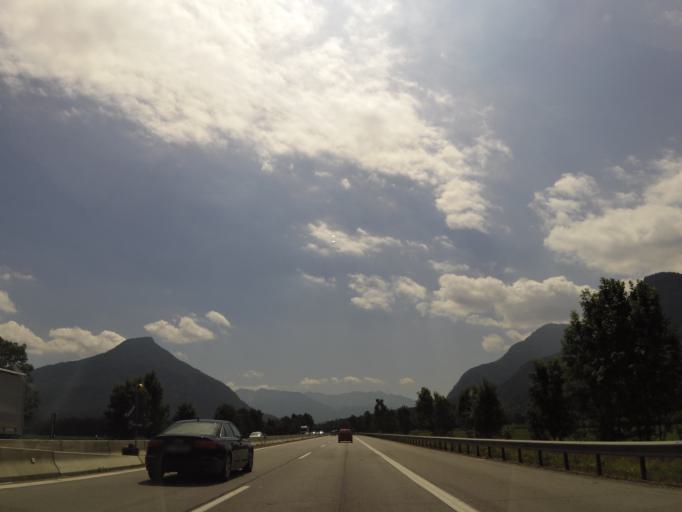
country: DE
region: Bavaria
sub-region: Upper Bavaria
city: Flintsbach
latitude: 47.7292
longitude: 12.1345
